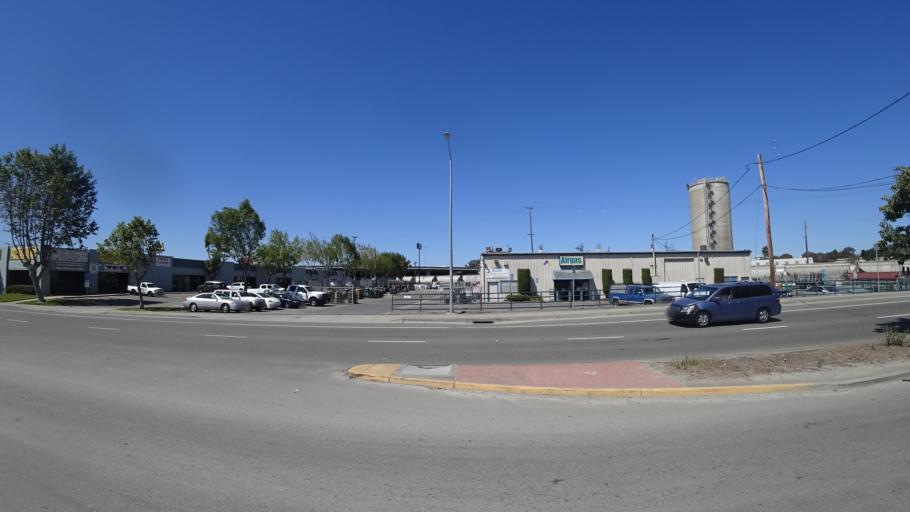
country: US
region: California
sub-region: Alameda County
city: Union City
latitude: 37.6101
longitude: -122.0666
